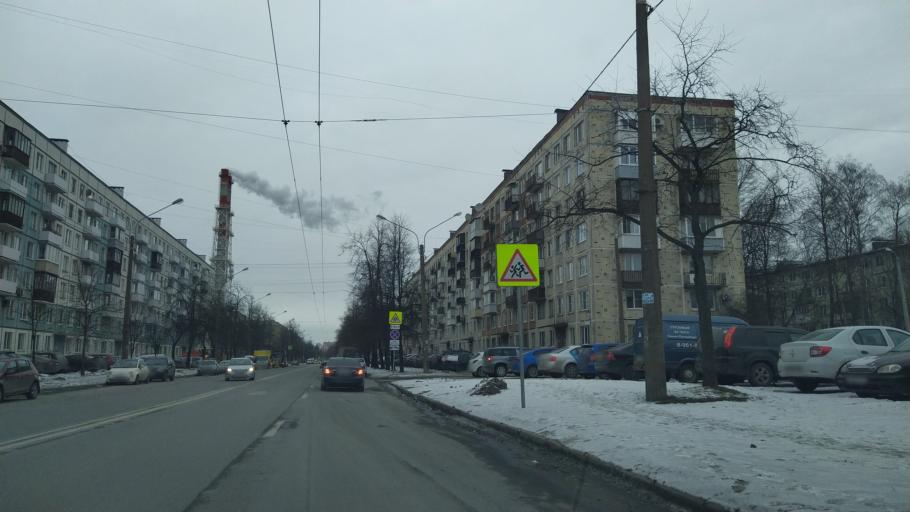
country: RU
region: Leningrad
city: Kalininskiy
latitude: 59.9542
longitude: 30.4221
